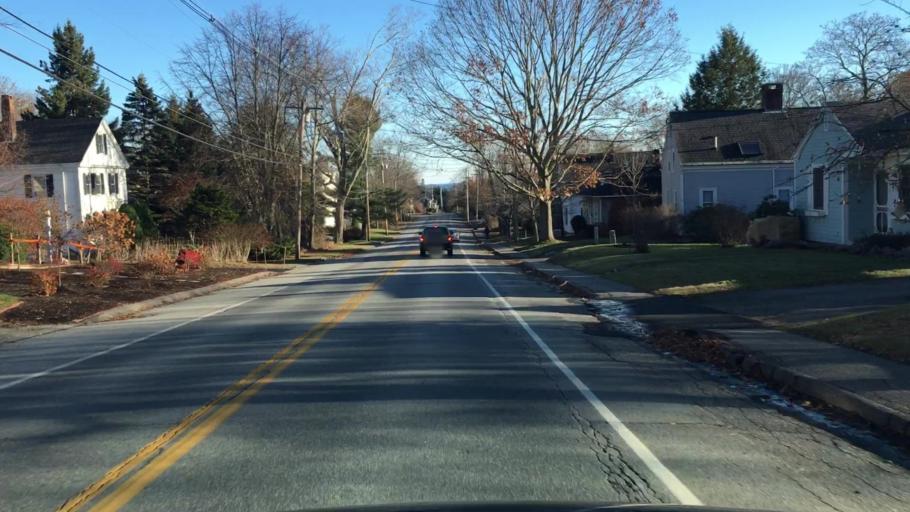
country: US
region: Maine
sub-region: Knox County
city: Camden
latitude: 44.2144
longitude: -69.0685
